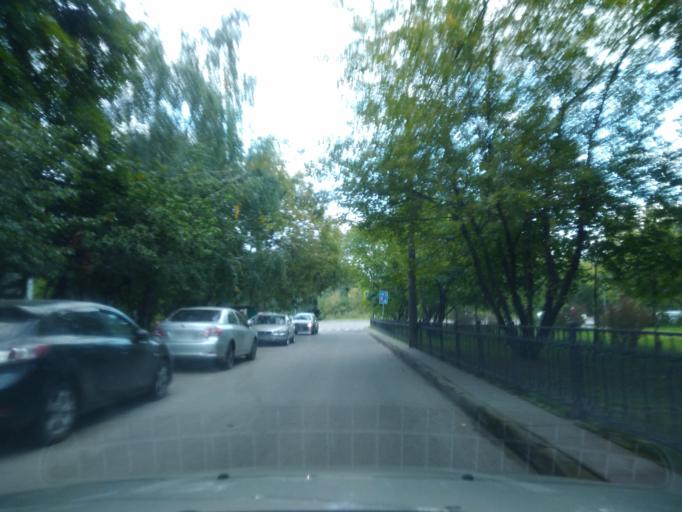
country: RU
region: Moscow
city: Strogino
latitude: 55.8177
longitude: 37.4020
